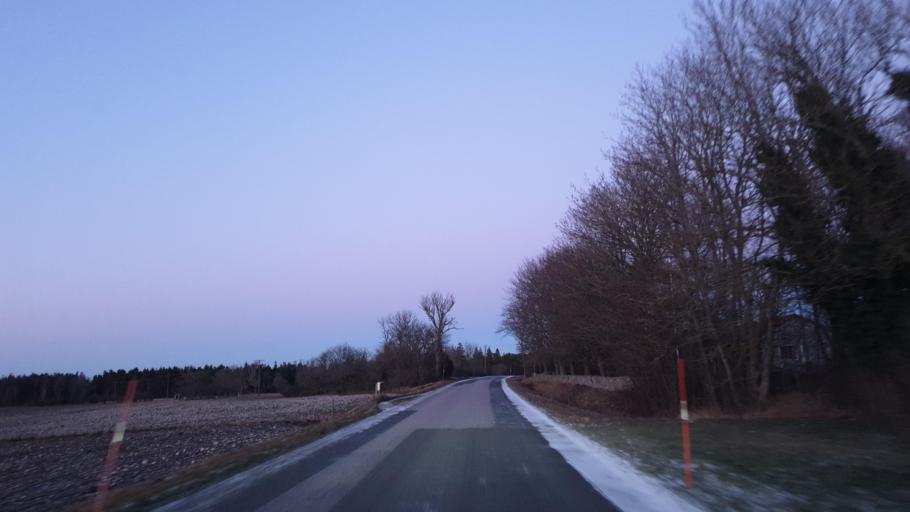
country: SE
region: Gotland
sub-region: Gotland
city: Slite
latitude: 57.4077
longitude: 18.8058
